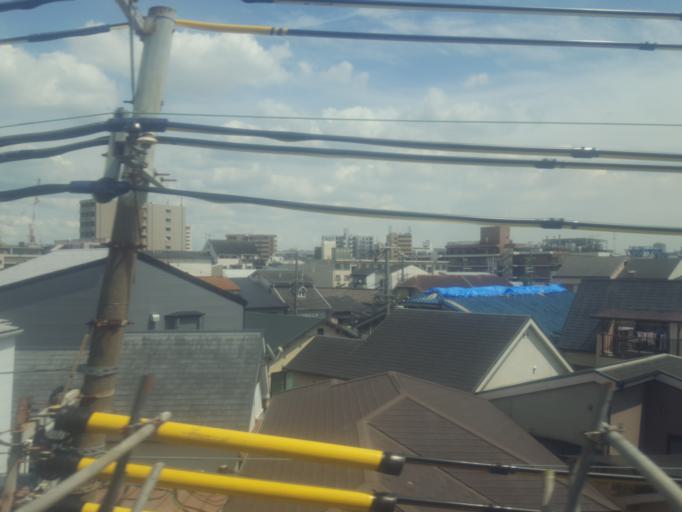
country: JP
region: Osaka
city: Suita
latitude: 34.7403
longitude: 135.5118
